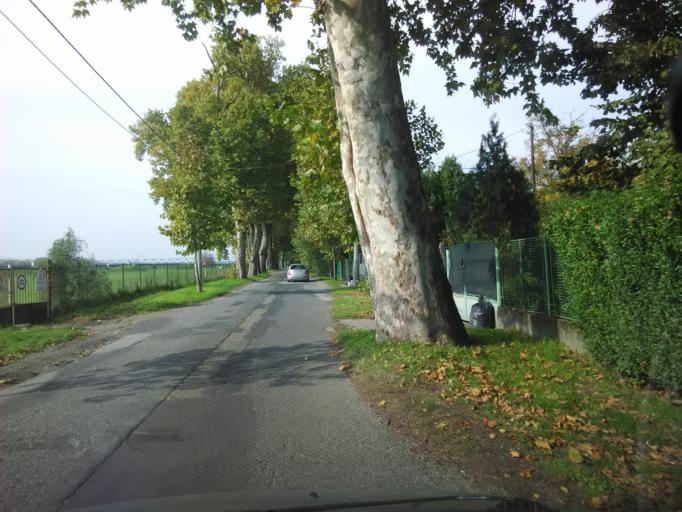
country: SK
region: Nitriansky
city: Komarno
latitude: 47.7566
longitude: 18.1022
